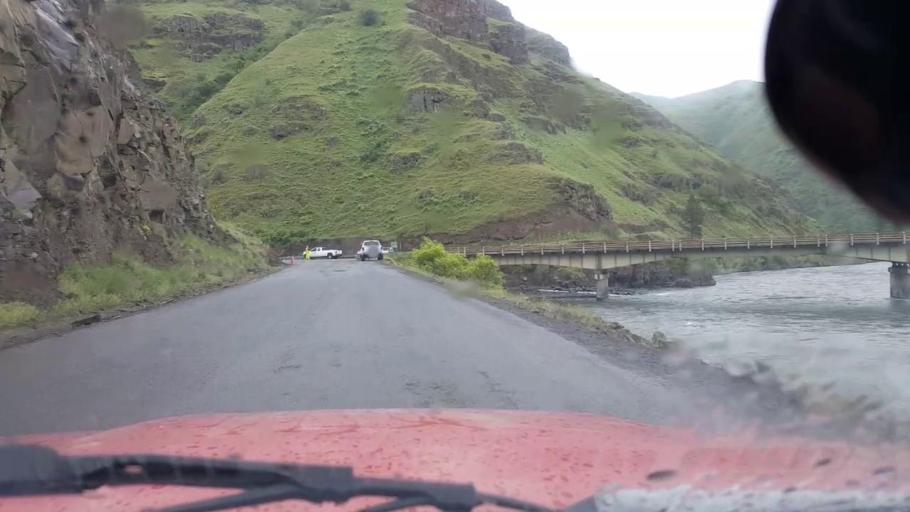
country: US
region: Washington
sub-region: Asotin County
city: Asotin
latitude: 46.0425
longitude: -117.2528
